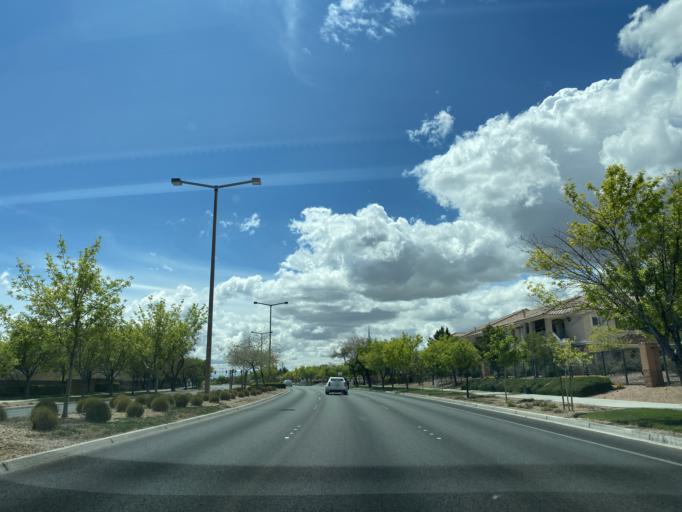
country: US
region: Nevada
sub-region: Clark County
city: Summerlin South
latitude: 36.1702
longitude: -115.3251
